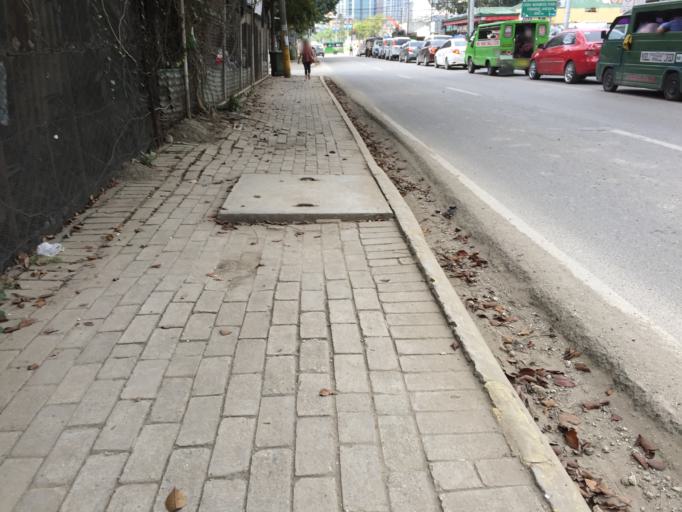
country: PH
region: Central Visayas
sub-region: Cebu City
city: Baugo
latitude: 10.3211
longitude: 123.9116
